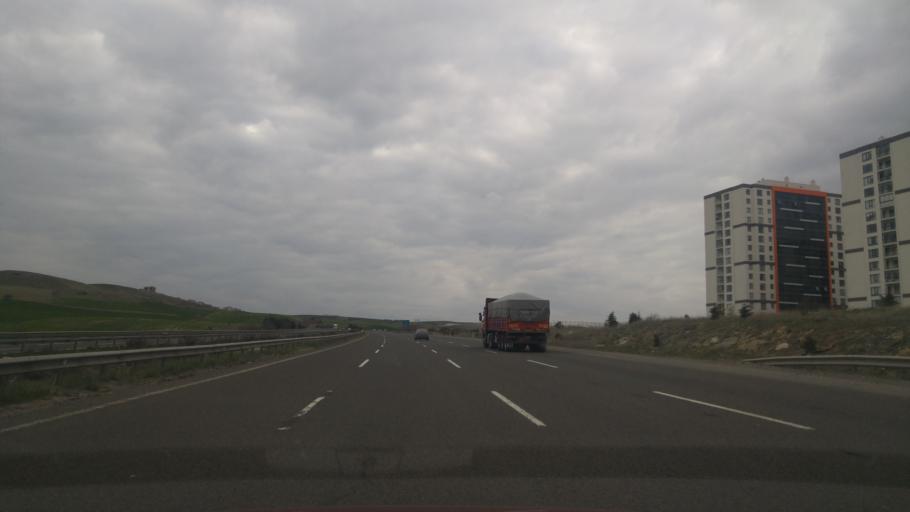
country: TR
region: Ankara
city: Etimesgut
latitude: 39.8439
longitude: 32.6381
